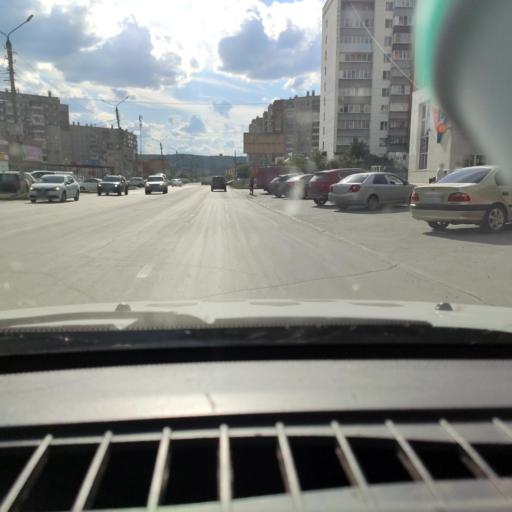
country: RU
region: Chelyabinsk
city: Miass
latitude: 55.0455
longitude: 60.1007
